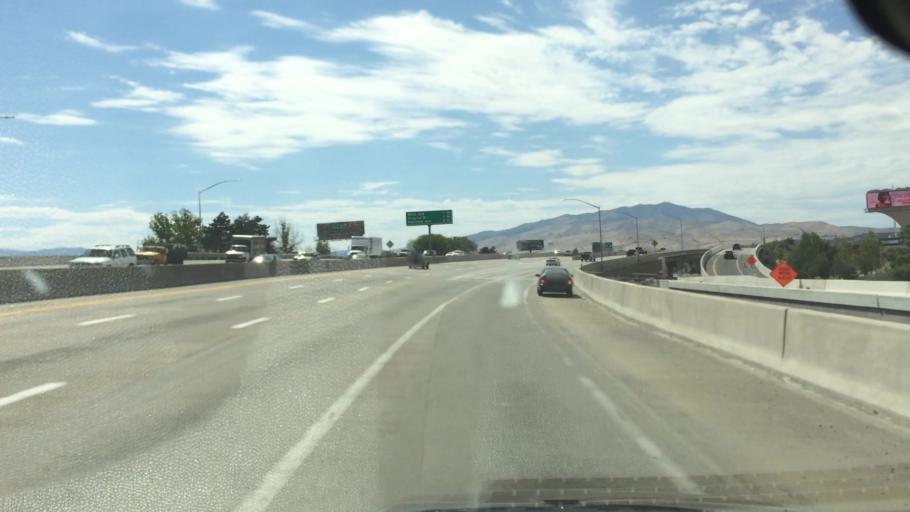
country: US
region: Nevada
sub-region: Washoe County
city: Sparks
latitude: 39.5345
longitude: -119.7756
